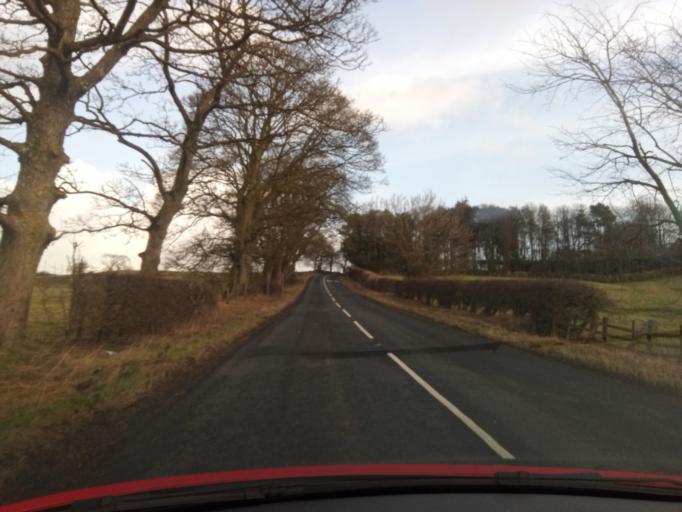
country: GB
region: England
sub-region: Northumberland
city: Rothley
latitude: 55.1046
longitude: -2.0180
